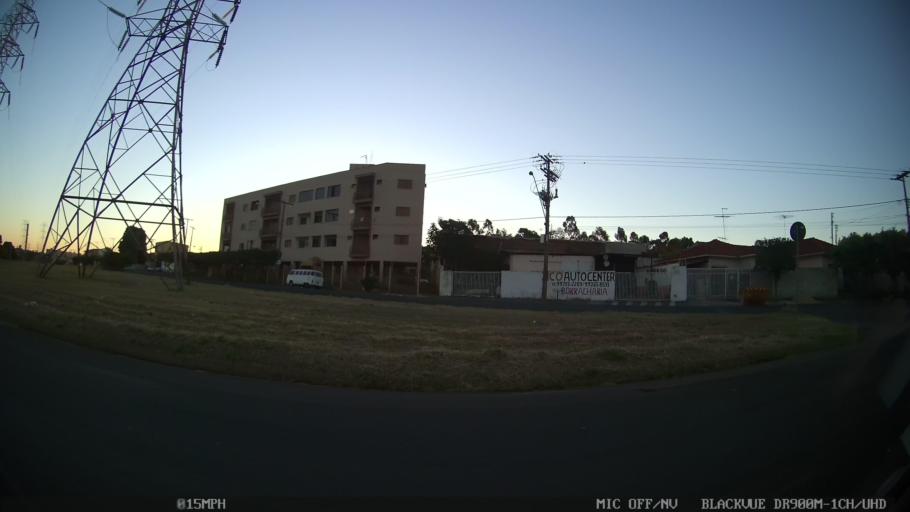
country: BR
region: Sao Paulo
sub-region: Sao Jose Do Rio Preto
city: Sao Jose do Rio Preto
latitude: -20.8422
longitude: -49.3741
